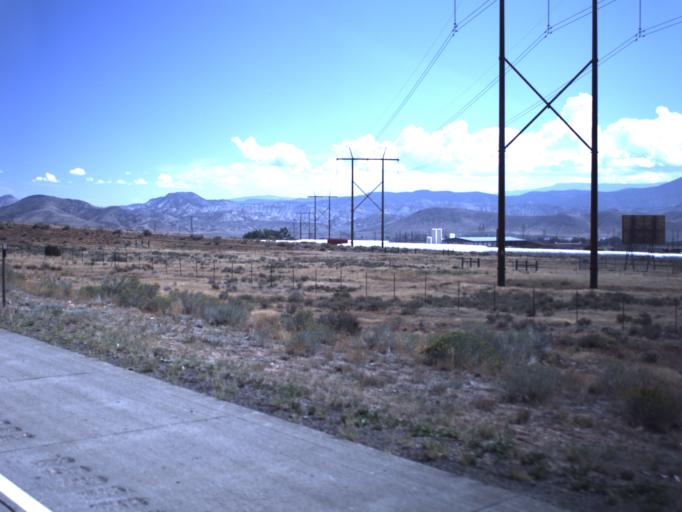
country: US
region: Utah
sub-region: Sevier County
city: Richfield
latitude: 38.8463
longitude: -112.0102
